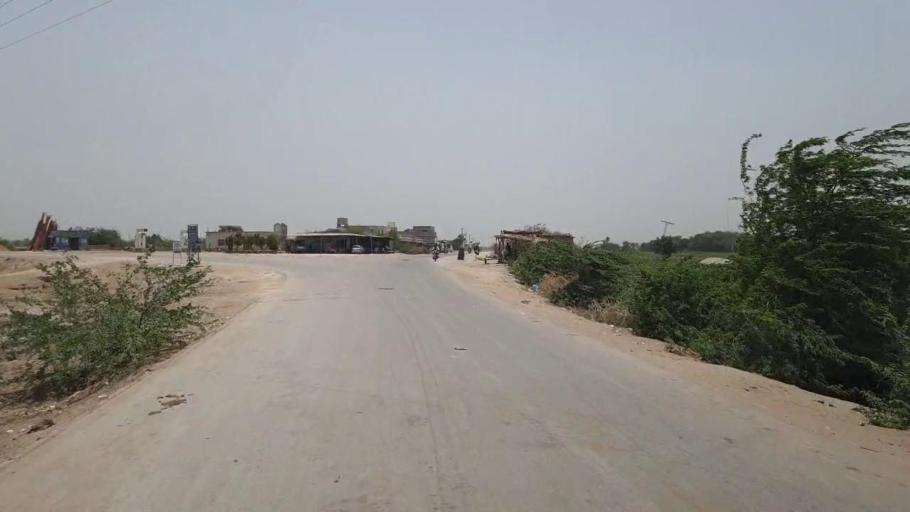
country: PK
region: Sindh
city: Tando Mittha Khan
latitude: 26.0557
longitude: 69.1921
